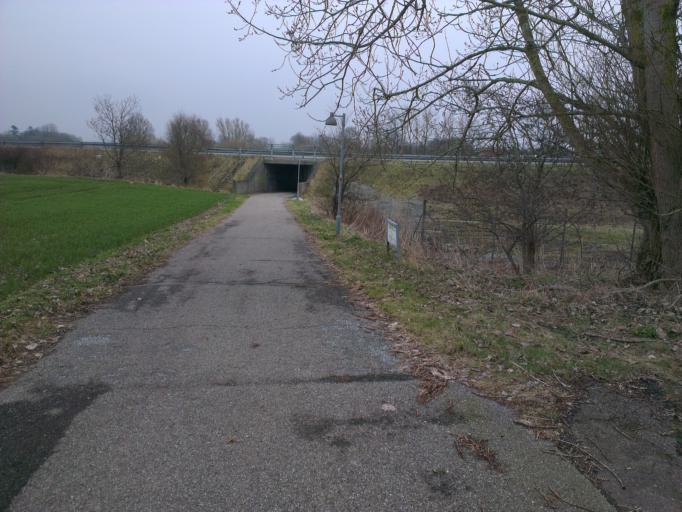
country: DK
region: Capital Region
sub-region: Frederikssund Kommune
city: Frederikssund
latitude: 55.8162
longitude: 12.1033
